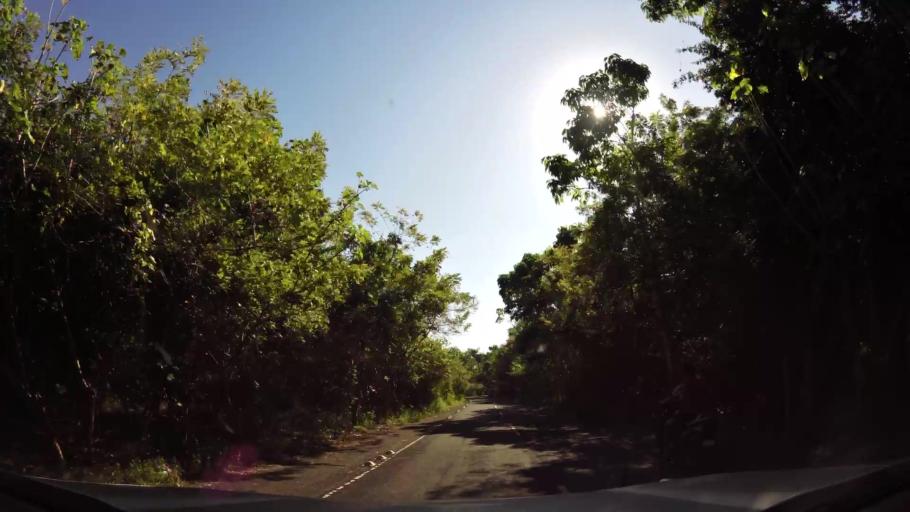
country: GT
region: Santa Rosa
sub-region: Municipio de Taxisco
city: Taxisco
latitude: 13.8898
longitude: -90.4753
